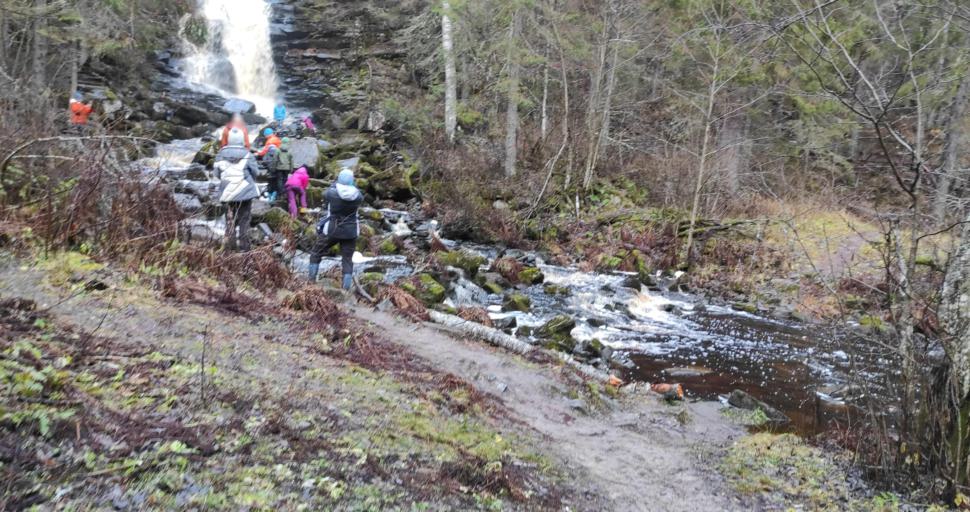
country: RU
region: Republic of Karelia
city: Pitkyaranta
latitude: 61.7537
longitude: 31.4118
